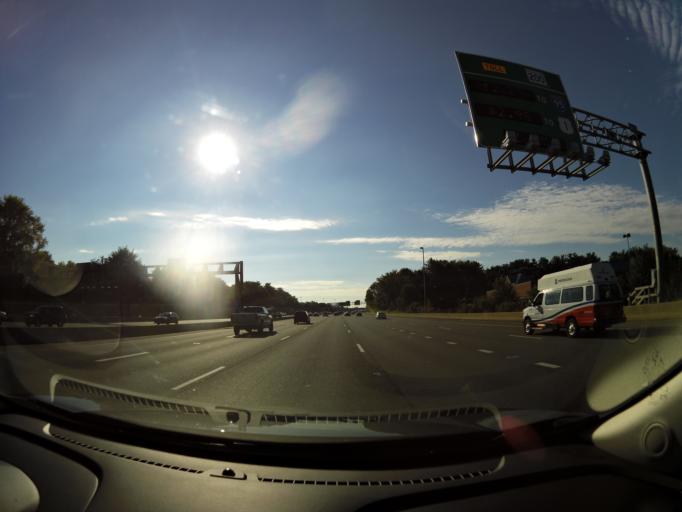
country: US
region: Maryland
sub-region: Montgomery County
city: Gaithersburg
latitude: 39.1293
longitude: -77.2047
